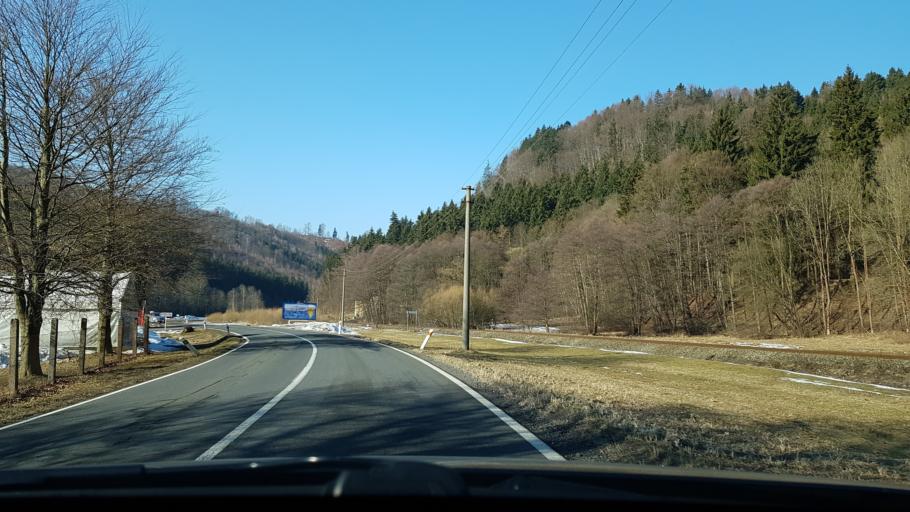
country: CZ
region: Olomoucky
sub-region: Okres Sumperk
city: Hanusovice
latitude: 50.0788
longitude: 16.9599
